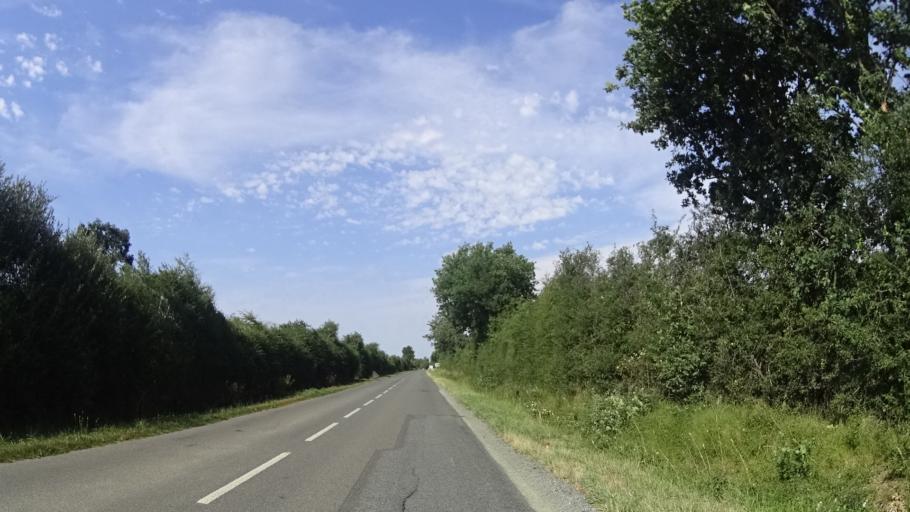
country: FR
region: Pays de la Loire
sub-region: Departement de la Loire-Atlantique
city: Saffre
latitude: 47.5055
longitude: -1.5650
